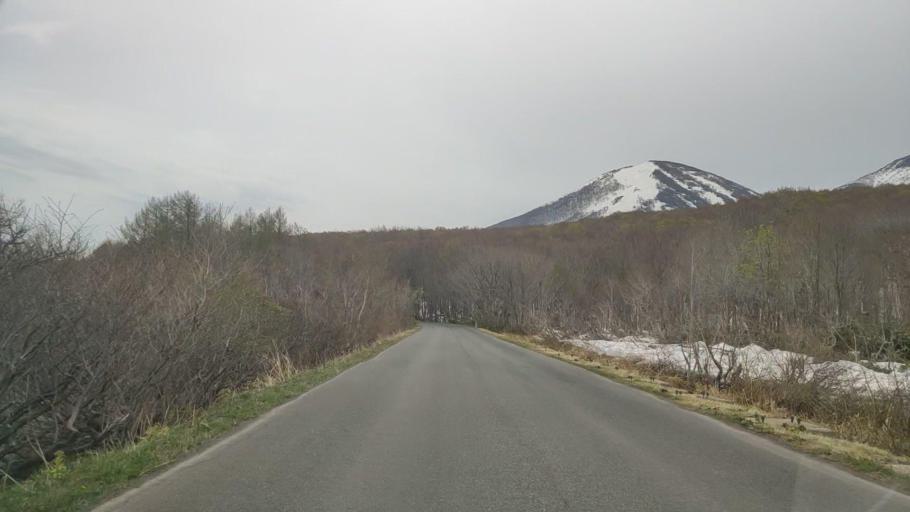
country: JP
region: Aomori
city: Aomori Shi
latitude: 40.6851
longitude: 140.9261
